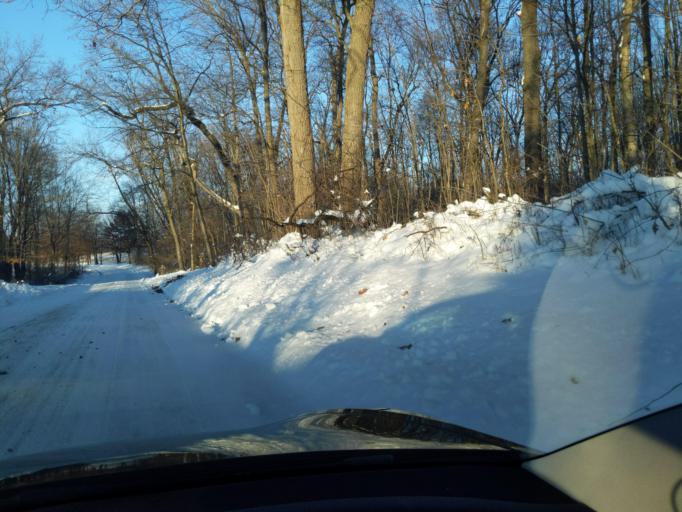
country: US
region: Michigan
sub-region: Ingham County
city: Stockbridge
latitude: 42.5086
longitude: -84.1174
